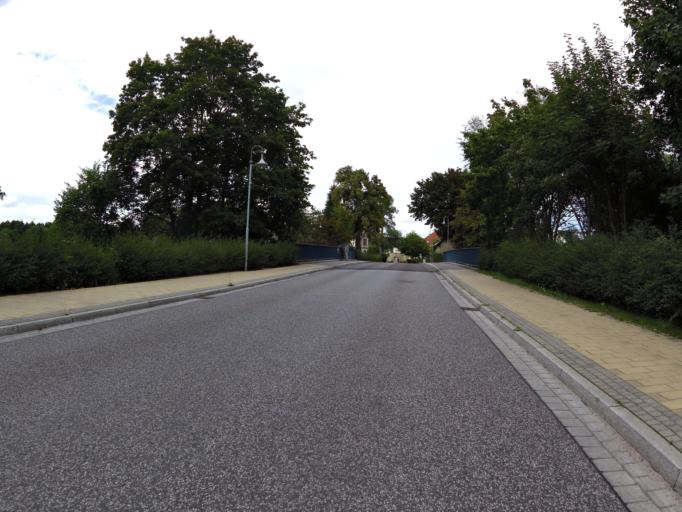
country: DE
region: Brandenburg
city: Wendisch Rietz
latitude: 52.2137
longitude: 14.0048
